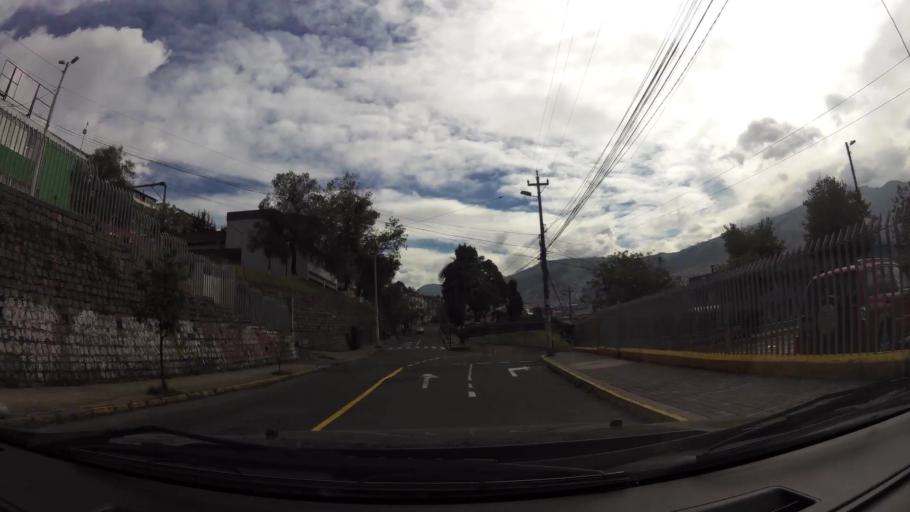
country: EC
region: Pichincha
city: Quito
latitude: -0.2173
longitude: -78.4981
